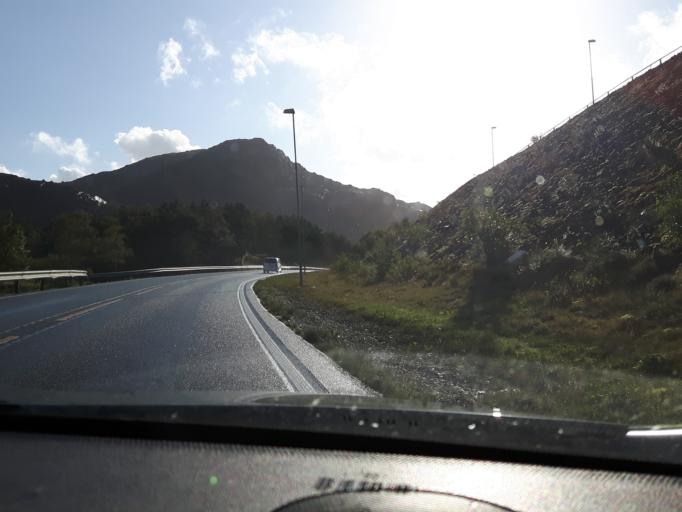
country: NO
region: Rogaland
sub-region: Gjesdal
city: Algard
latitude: 58.7540
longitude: 5.9146
